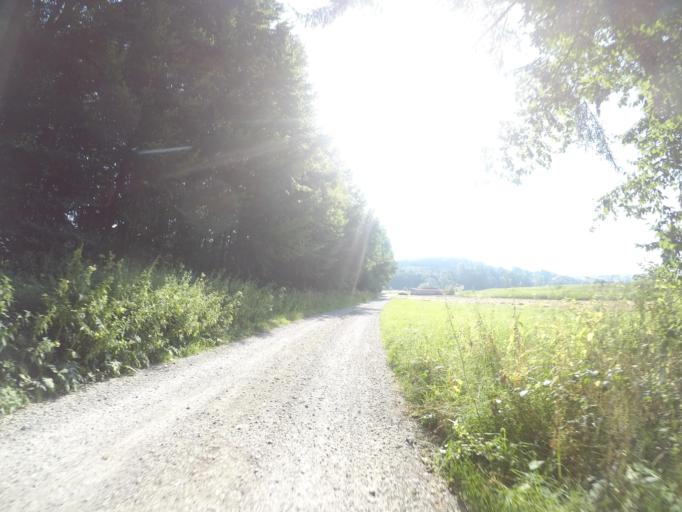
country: DE
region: Baden-Wuerttemberg
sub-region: Tuebingen Region
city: Schnurpflingen
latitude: 48.2388
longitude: 10.0103
